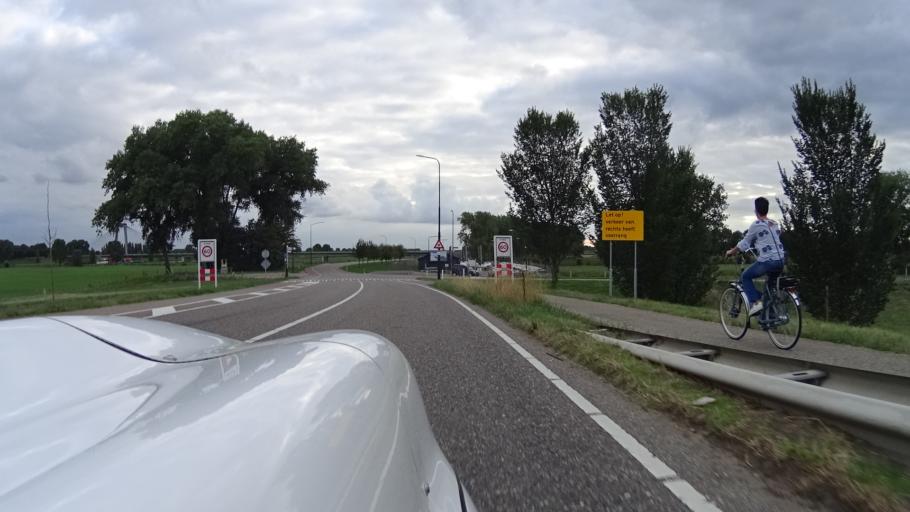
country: NL
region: North Brabant
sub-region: Gemeente Aalburg
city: Aalburg
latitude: 51.7419
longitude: 5.1233
